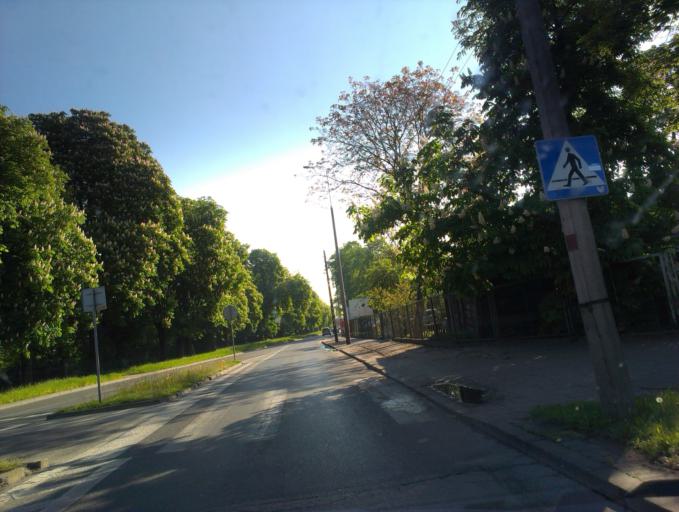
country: PL
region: Masovian Voivodeship
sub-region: Radom
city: Radom
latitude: 51.3934
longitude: 21.1599
